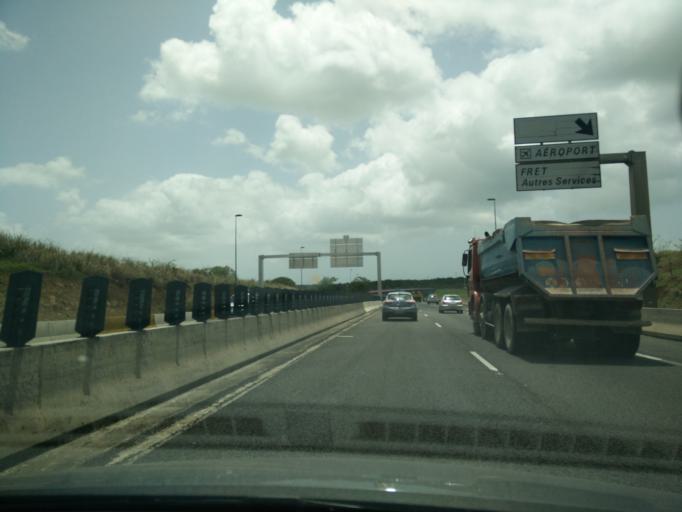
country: GP
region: Guadeloupe
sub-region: Guadeloupe
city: Les Abymes
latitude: 16.2732
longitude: -61.5170
